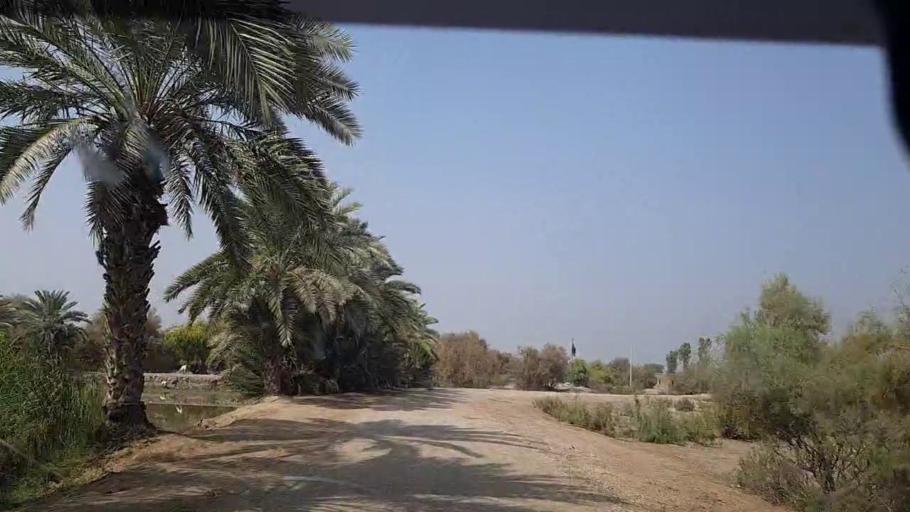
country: PK
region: Sindh
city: Shikarpur
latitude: 28.0903
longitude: 68.6688
